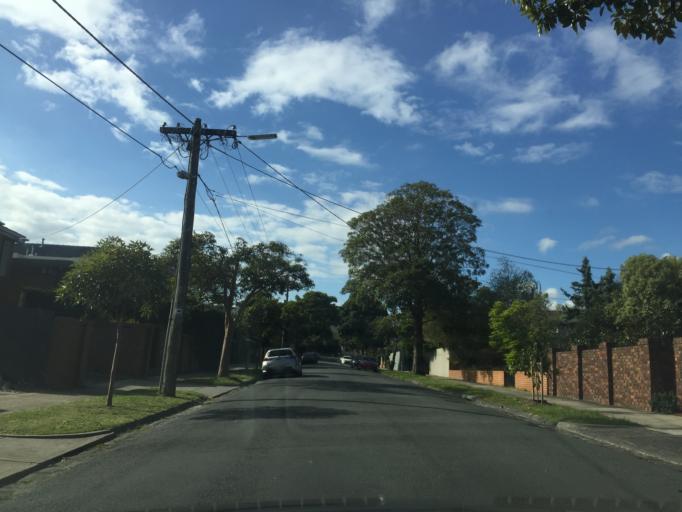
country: AU
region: Victoria
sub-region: Glen Eira
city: Caulfield North
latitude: -37.8662
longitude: 145.0170
